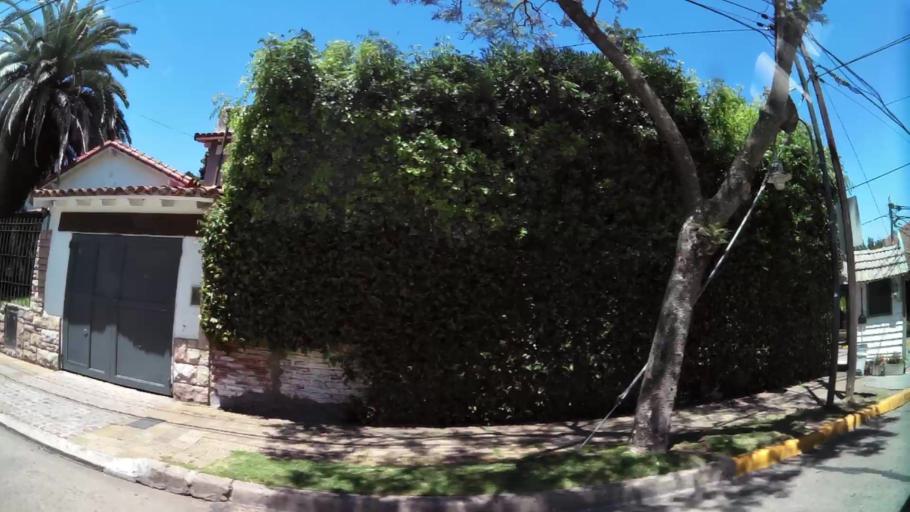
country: AR
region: Buenos Aires
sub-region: Partido de Tigre
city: Tigre
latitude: -34.4422
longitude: -58.5503
